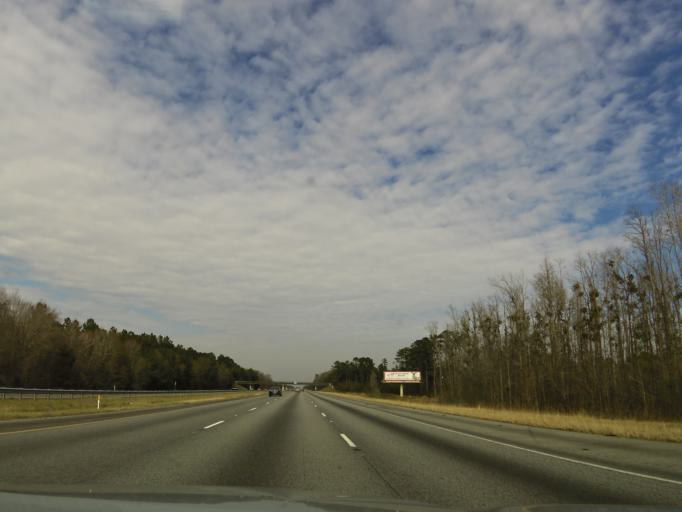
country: US
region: Georgia
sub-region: Liberty County
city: Midway
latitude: 31.5958
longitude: -81.4236
